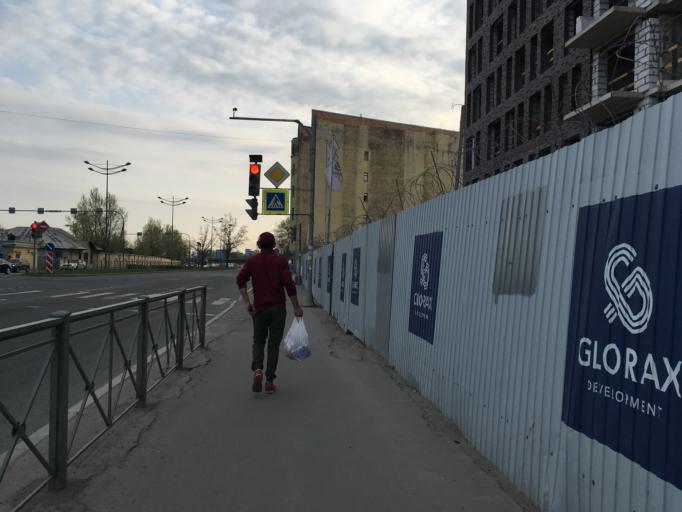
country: RU
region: St.-Petersburg
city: Centralniy
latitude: 59.9052
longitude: 30.3426
